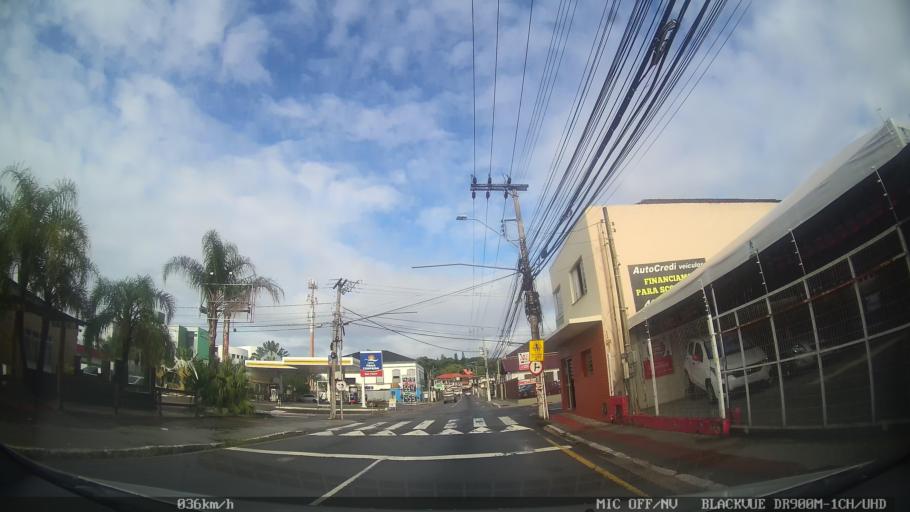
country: BR
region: Santa Catarina
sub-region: Sao Jose
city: Campinas
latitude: -27.6075
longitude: -48.6271
